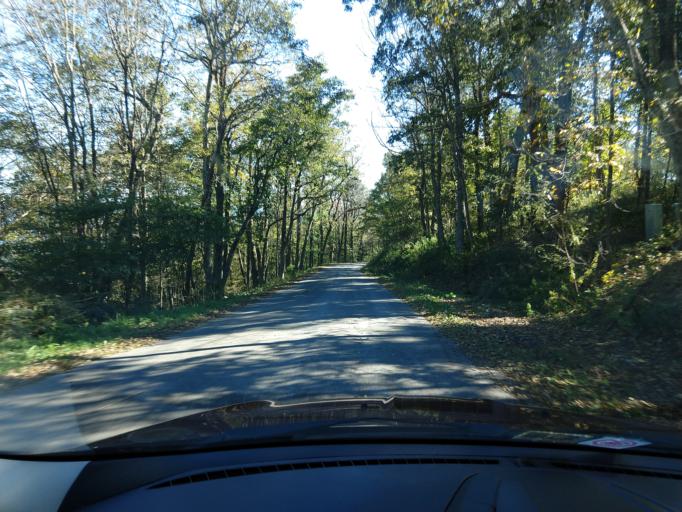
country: US
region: Virginia
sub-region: Alleghany County
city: Clifton Forge
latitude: 37.8746
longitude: -79.8872
